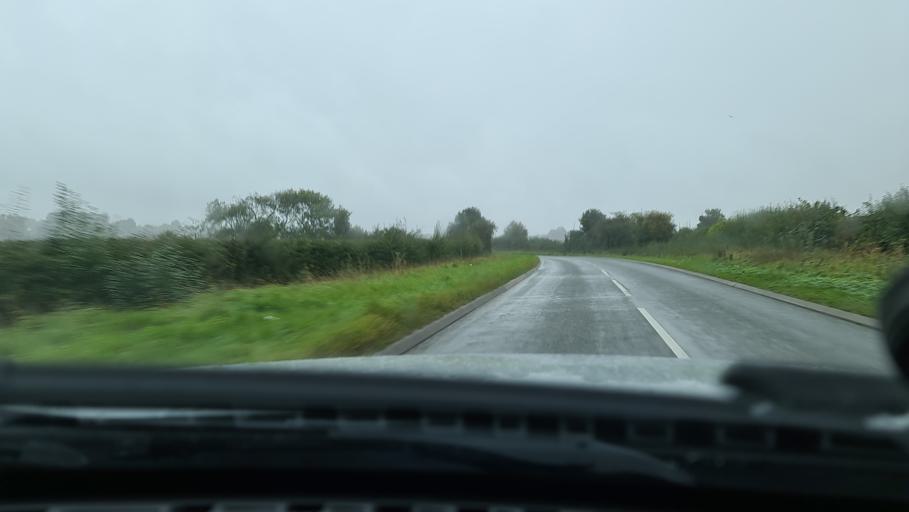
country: GB
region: England
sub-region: Oxfordshire
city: Somerton
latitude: 51.9229
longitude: -1.2803
